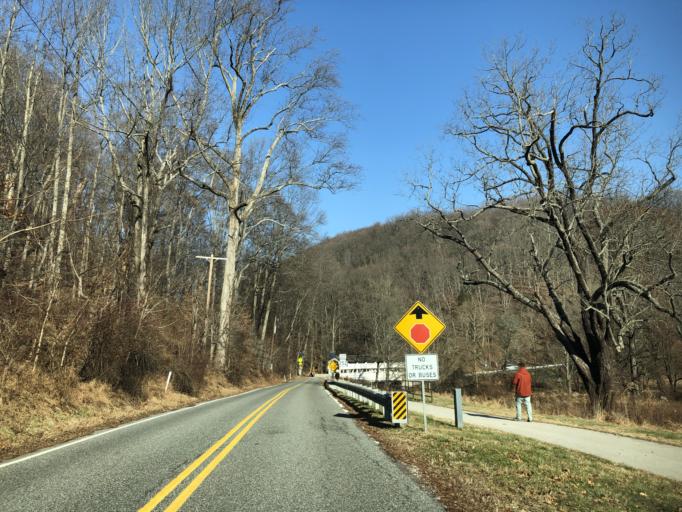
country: US
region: Pennsylvania
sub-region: Chester County
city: Chesterbrook
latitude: 40.0861
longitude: -75.4572
